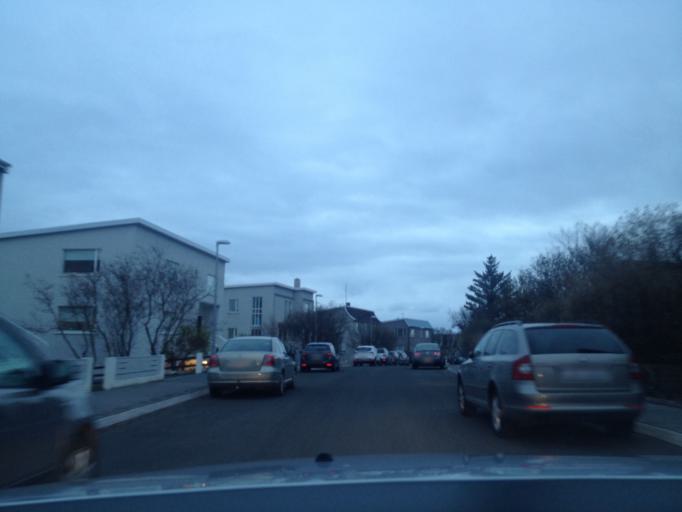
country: IS
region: Capital Region
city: Seltjarnarnes
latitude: 64.1526
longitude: -21.9995
